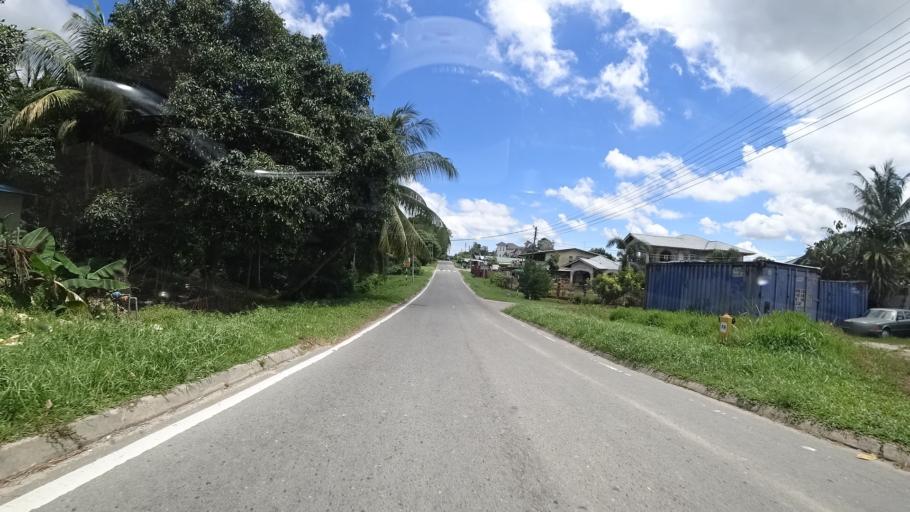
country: BN
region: Brunei and Muara
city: Bandar Seri Begawan
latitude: 4.9413
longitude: 114.9503
